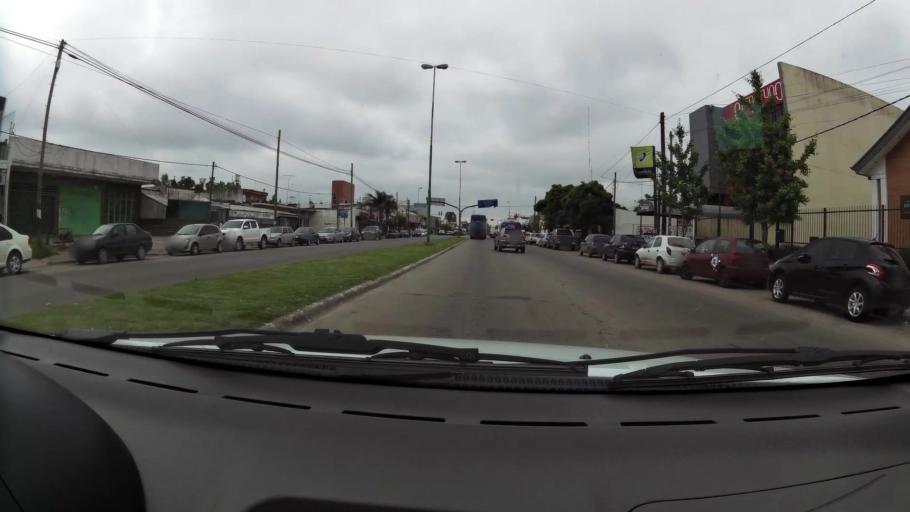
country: AR
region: Buenos Aires
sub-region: Partido de La Plata
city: La Plata
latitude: -34.9963
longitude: -58.0492
